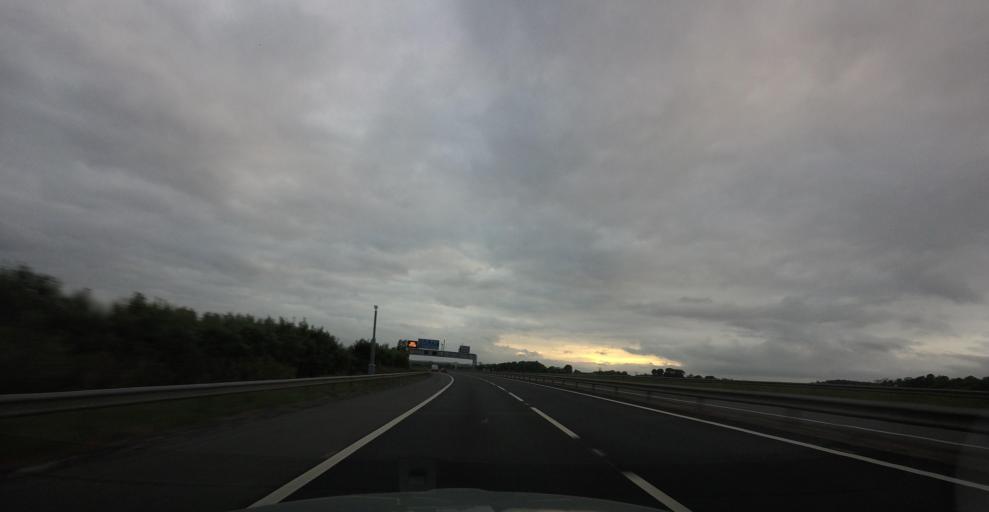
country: GB
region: Scotland
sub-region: Edinburgh
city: Kirkliston
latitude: 55.9644
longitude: -3.4070
